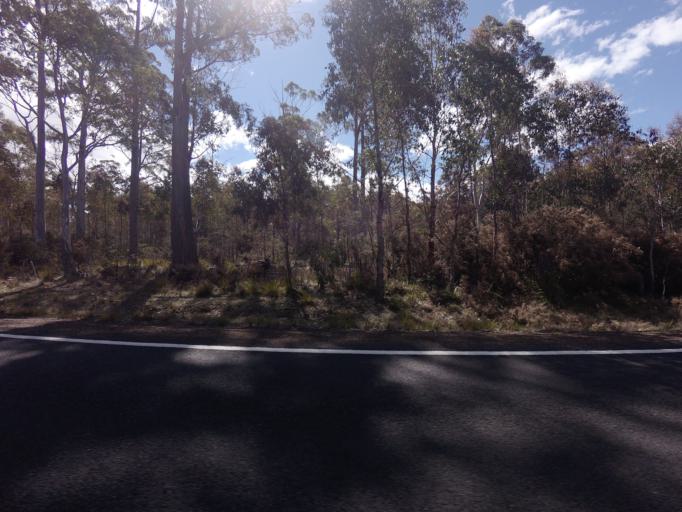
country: AU
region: Tasmania
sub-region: Northern Midlands
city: Evandale
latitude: -42.0340
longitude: 147.8193
